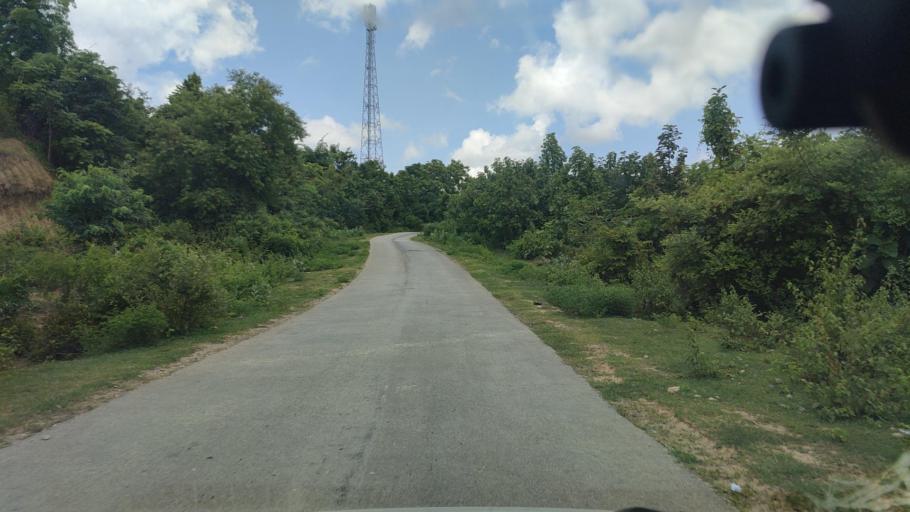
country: MM
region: Magway
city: Taungdwingyi
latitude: 20.0144
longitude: 95.8348
